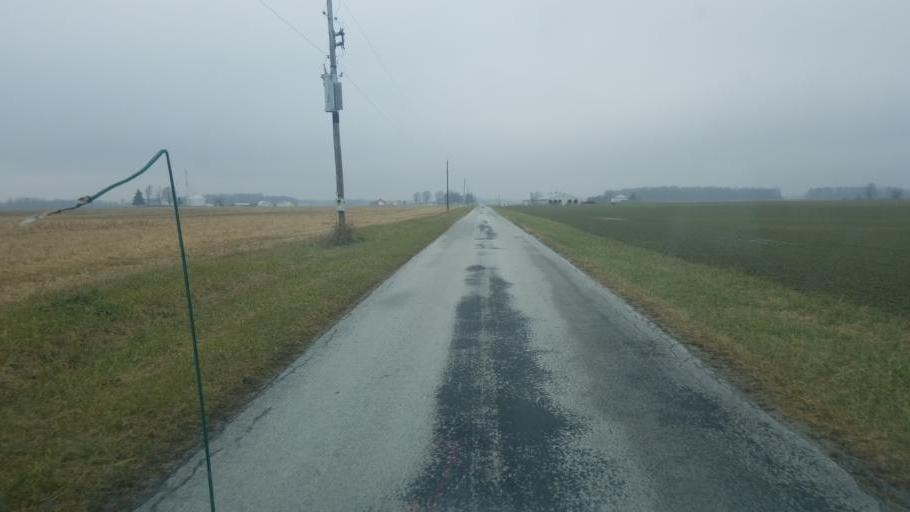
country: US
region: Ohio
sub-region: Hardin County
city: Forest
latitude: 40.6875
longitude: -83.4778
